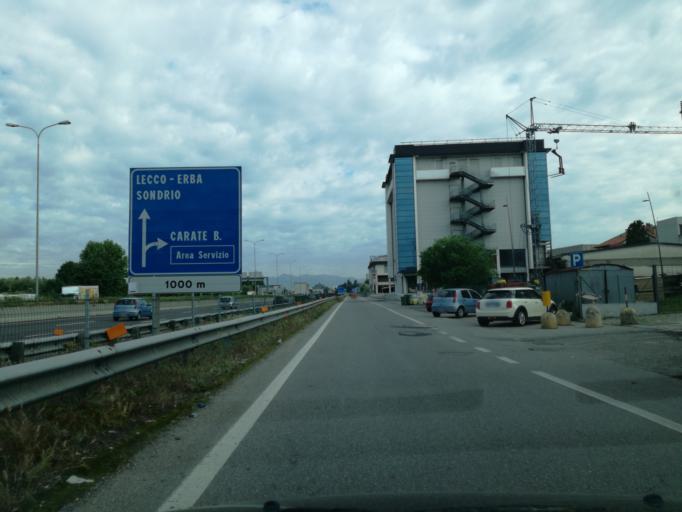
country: IT
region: Lombardy
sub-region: Provincia di Monza e Brianza
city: Santa Margherita
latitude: 45.6501
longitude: 9.2260
